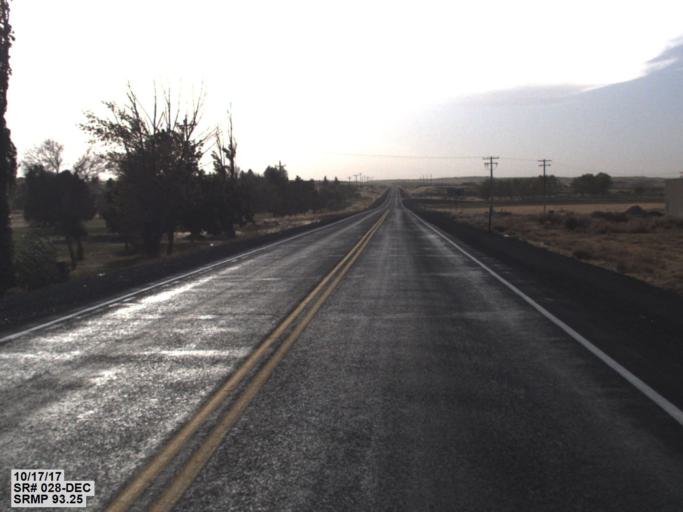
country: US
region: Washington
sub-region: Adams County
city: Ritzville
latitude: 47.3317
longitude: -118.7016
